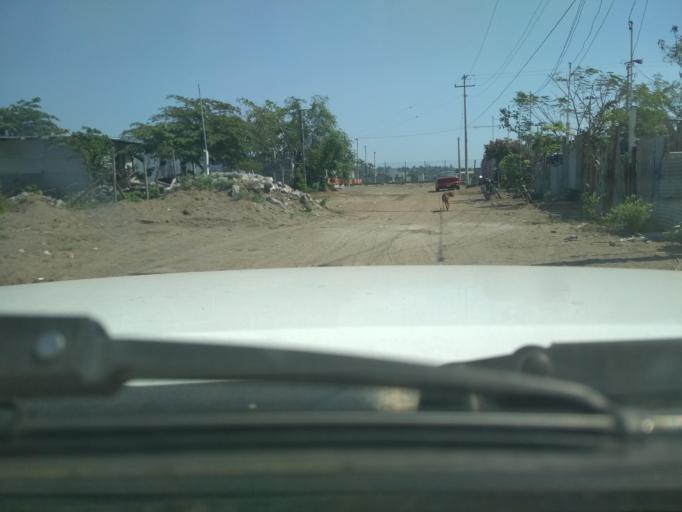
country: MX
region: Veracruz
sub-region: Veracruz
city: Lomas de Rio Medio Cuatro
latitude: 19.1922
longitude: -96.1999
